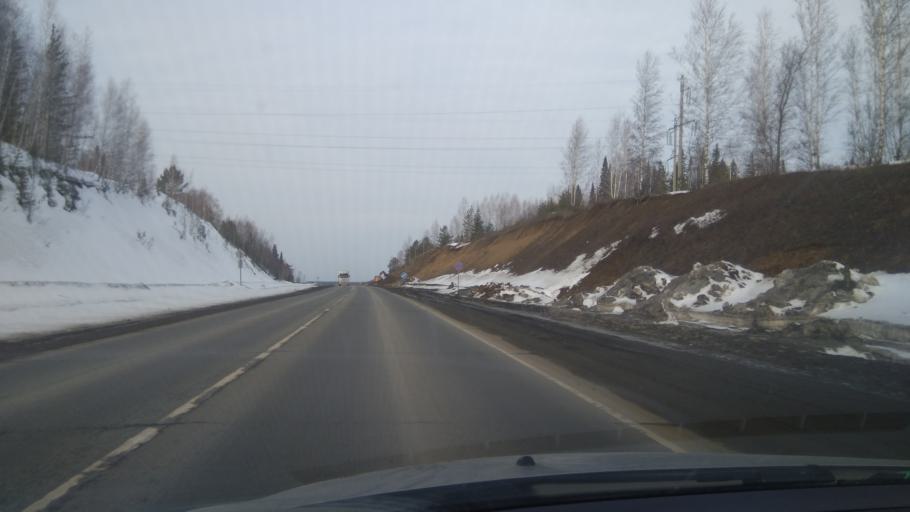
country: RU
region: Sverdlovsk
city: Bisert'
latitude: 56.8298
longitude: 59.0814
